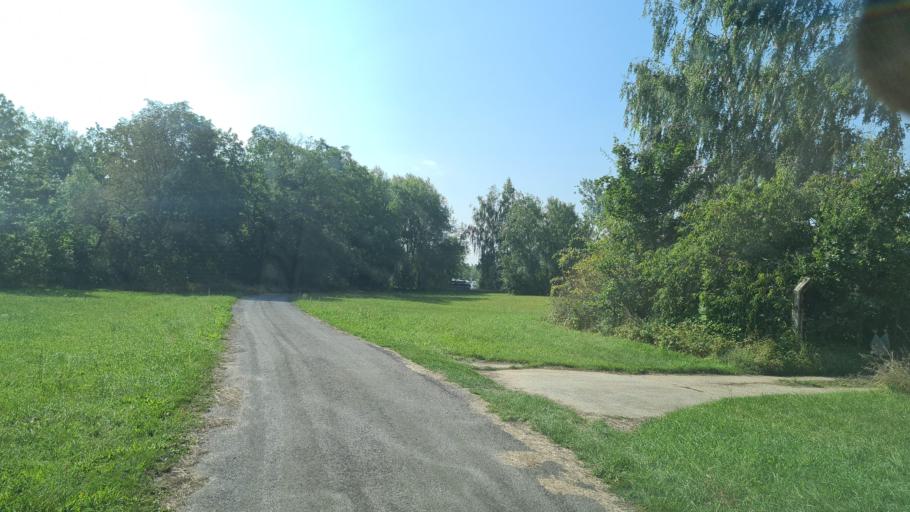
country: DE
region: Brandenburg
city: Luckau
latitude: 51.8426
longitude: 13.6831
